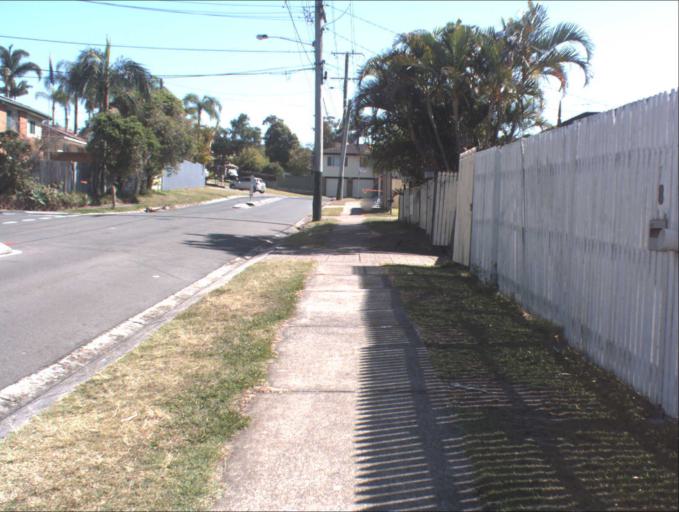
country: AU
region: Queensland
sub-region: Logan
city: Springwood
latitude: -27.6042
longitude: 153.1263
